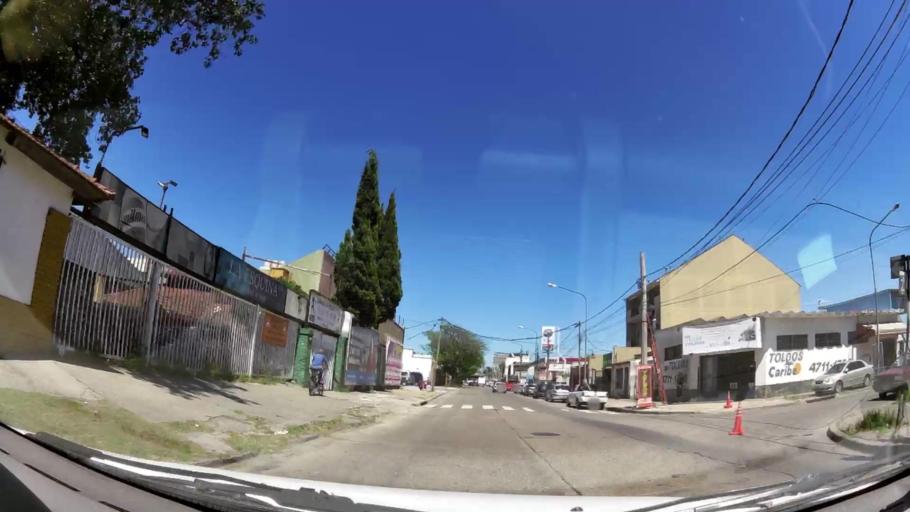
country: AR
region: Buenos Aires
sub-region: Partido de Vicente Lopez
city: Olivos
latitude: -34.5173
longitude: -58.5120
